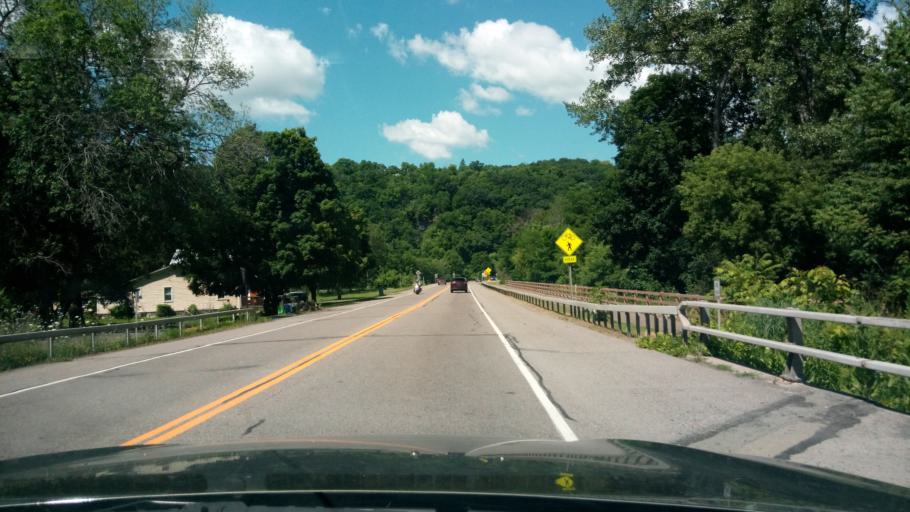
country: US
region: New York
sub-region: Schuyler County
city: Montour Falls
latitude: 42.3509
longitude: -76.8501
